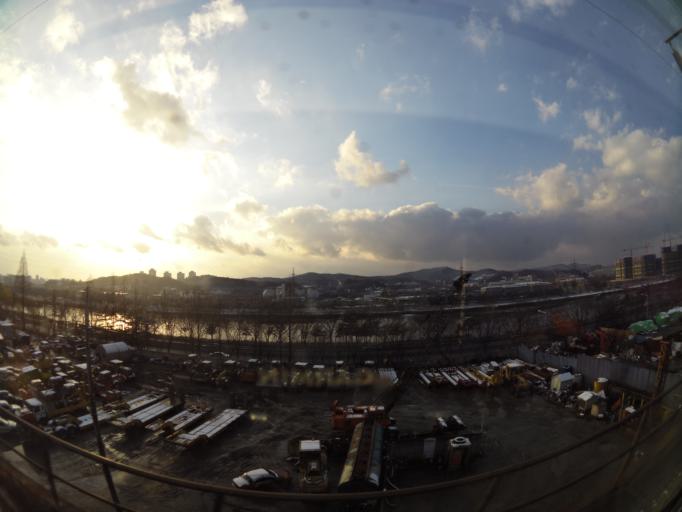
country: KR
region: Daejeon
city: Songgang-dong
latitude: 36.3867
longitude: 127.4136
